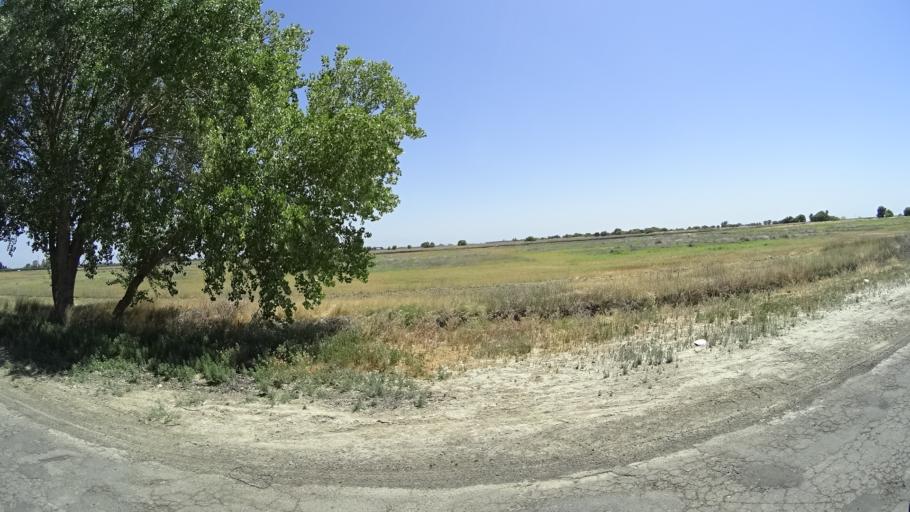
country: US
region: California
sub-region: Kings County
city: Lemoore
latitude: 36.2363
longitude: -119.7445
